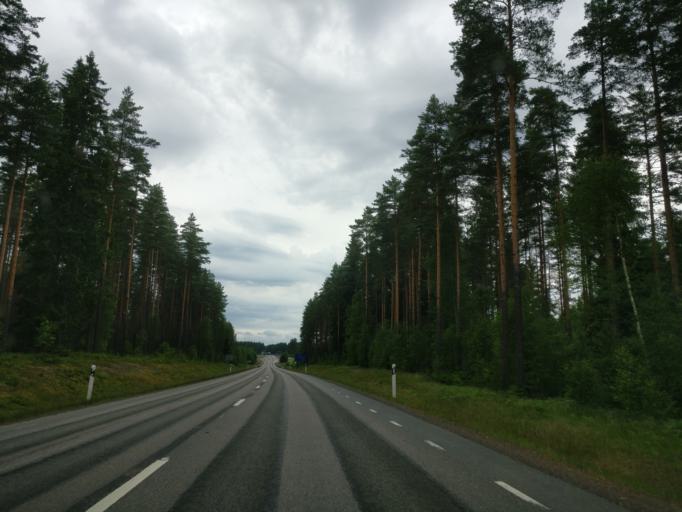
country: SE
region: Vaermland
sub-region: Hagfors Kommun
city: Hagfors
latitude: 60.0291
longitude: 13.5898
